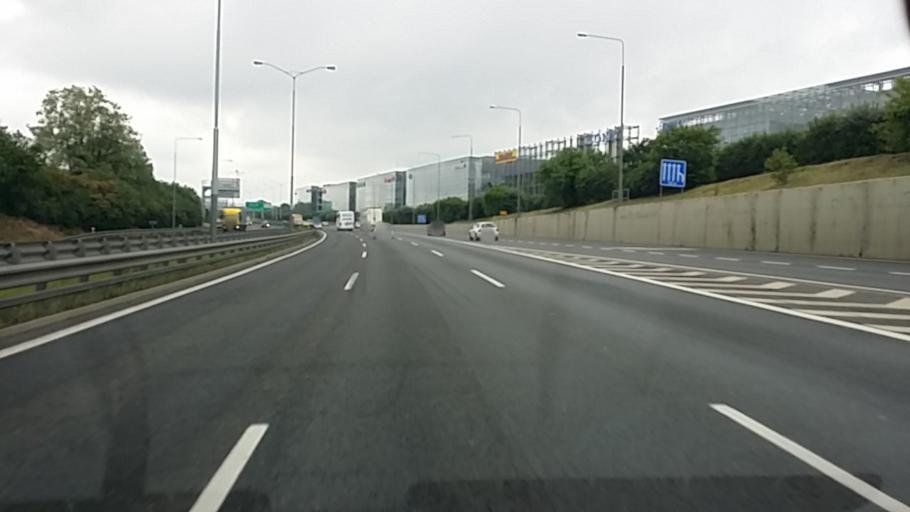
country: CZ
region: Central Bohemia
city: Vestec
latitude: 50.0301
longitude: 14.4941
